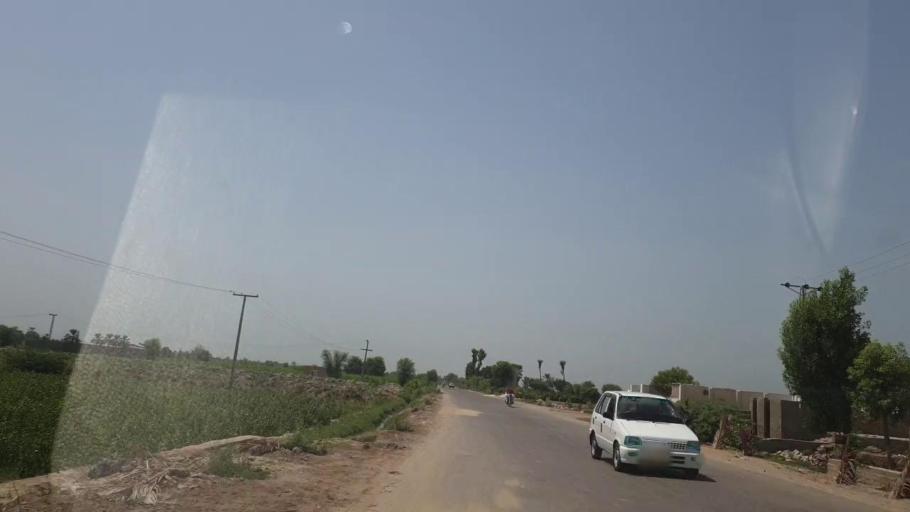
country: PK
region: Sindh
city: Gambat
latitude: 27.3005
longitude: 68.6056
